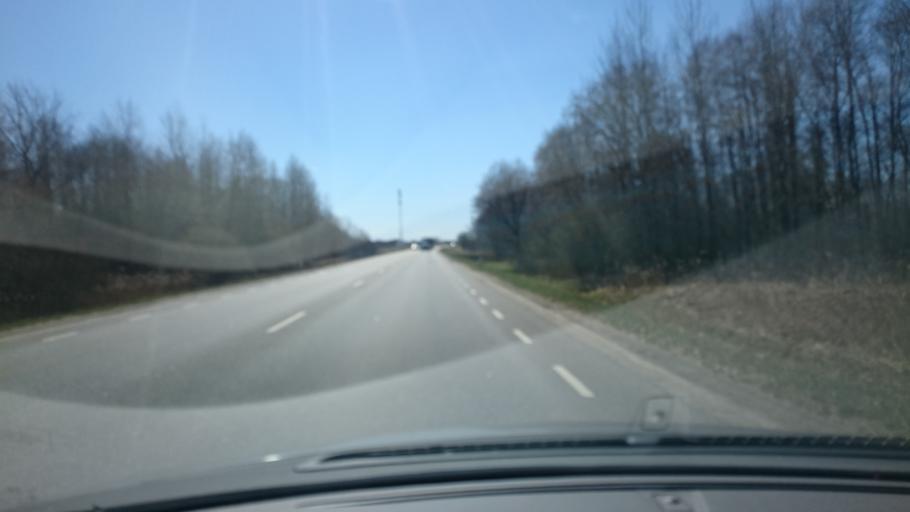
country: EE
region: Harju
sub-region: Rae vald
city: Jueri
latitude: 59.3667
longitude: 24.9040
